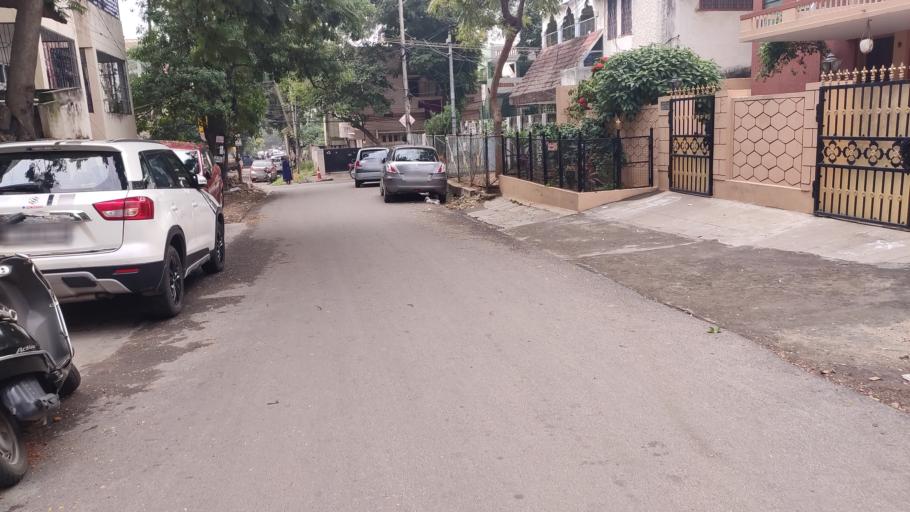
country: IN
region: Telangana
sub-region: Rangareddi
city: Kukatpalli
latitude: 17.4435
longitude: 78.4347
